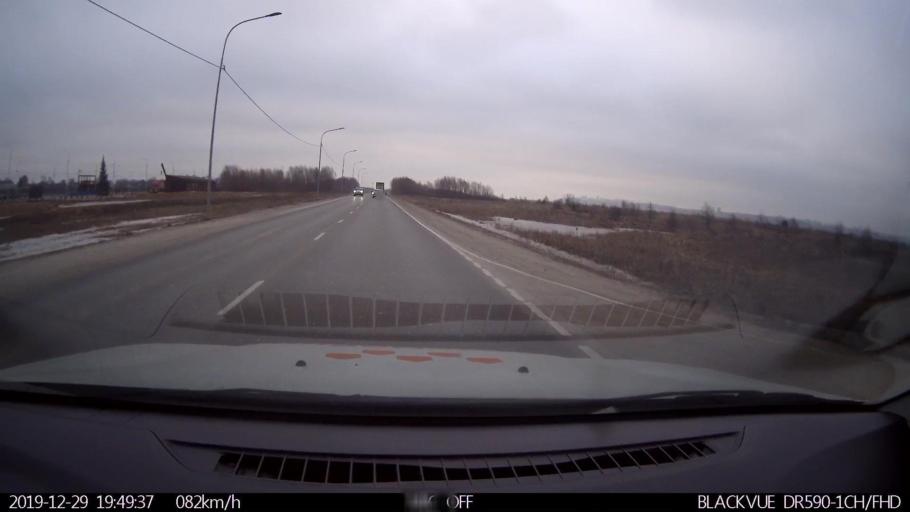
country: RU
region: Nizjnij Novgorod
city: Nizhniy Novgorod
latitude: 56.3751
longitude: 44.0149
